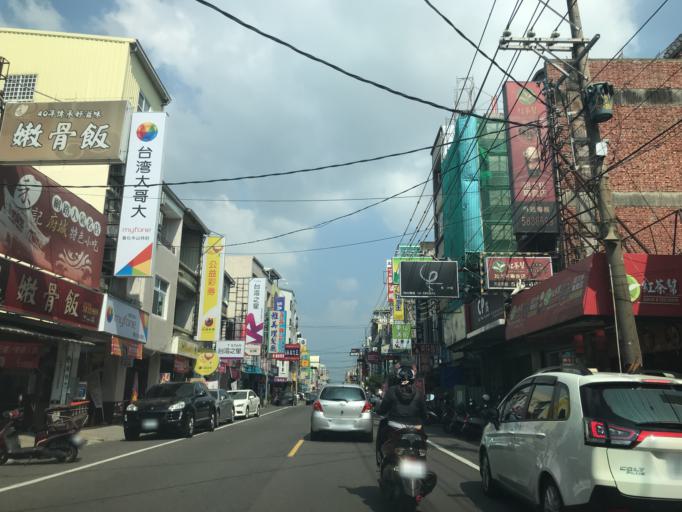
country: TW
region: Taiwan
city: Yujing
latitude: 23.1323
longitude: 120.2982
